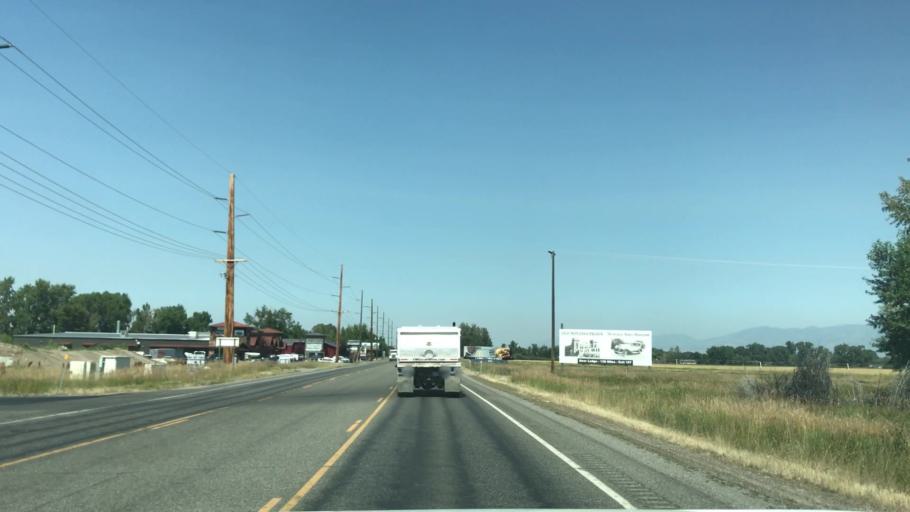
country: US
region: Montana
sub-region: Gallatin County
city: Four Corners
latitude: 45.6601
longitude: -111.1858
